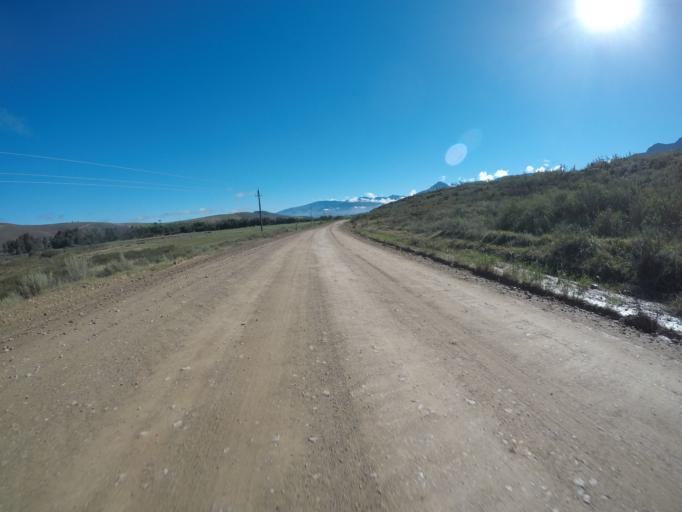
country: ZA
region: Western Cape
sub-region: Overberg District Municipality
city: Caledon
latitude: -34.0966
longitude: 19.6718
